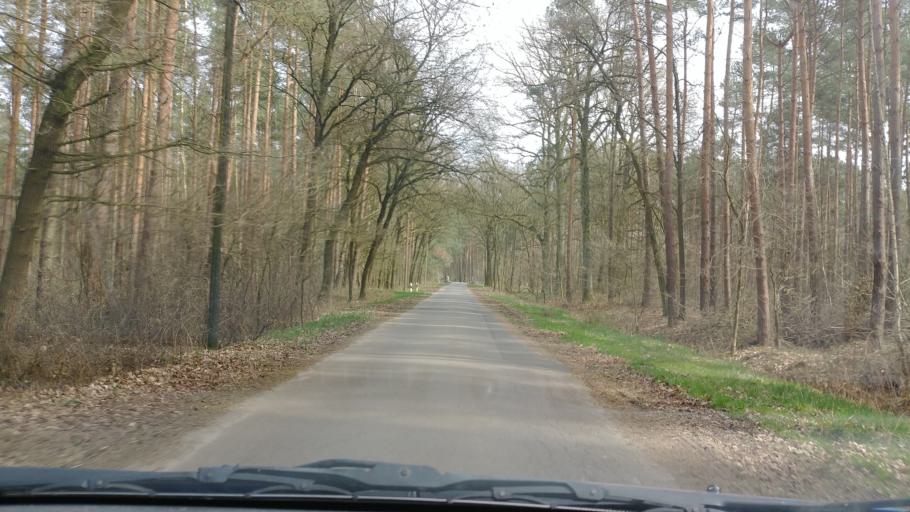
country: DE
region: Lower Saxony
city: Elze
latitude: 52.5638
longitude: 9.7978
